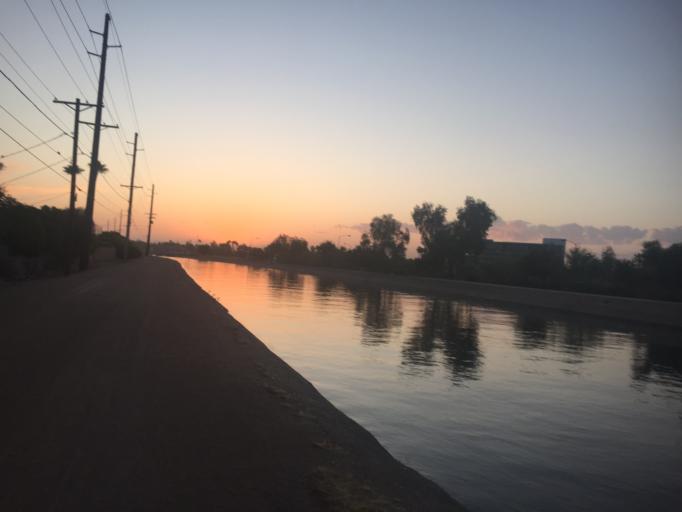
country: US
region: Arizona
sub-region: Maricopa County
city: Paradise Valley
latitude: 33.4933
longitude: -111.9380
